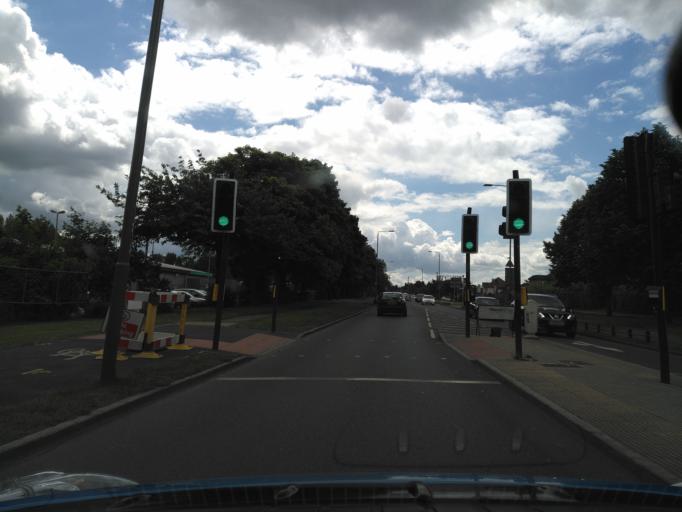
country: GB
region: England
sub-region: Greater London
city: Sidcup
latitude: 51.4071
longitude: 0.1133
